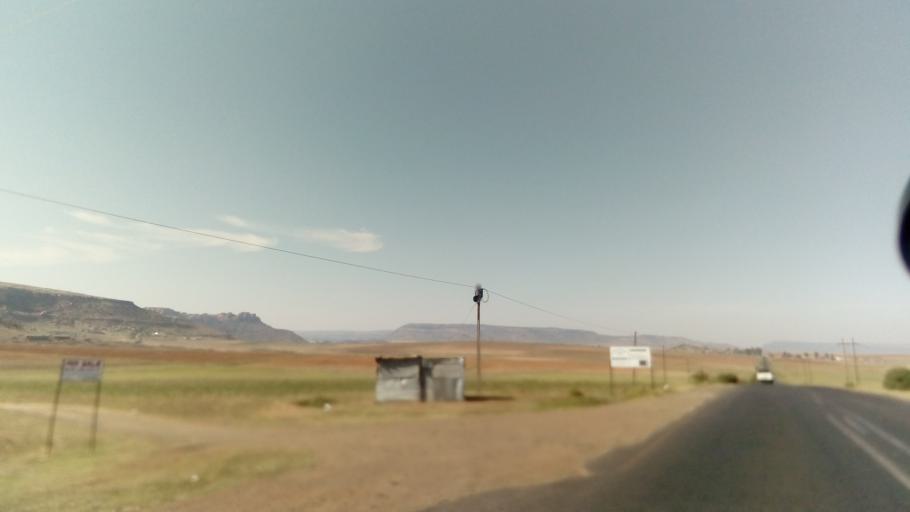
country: LS
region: Berea
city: Teyateyaneng
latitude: -29.1690
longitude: 27.6405
